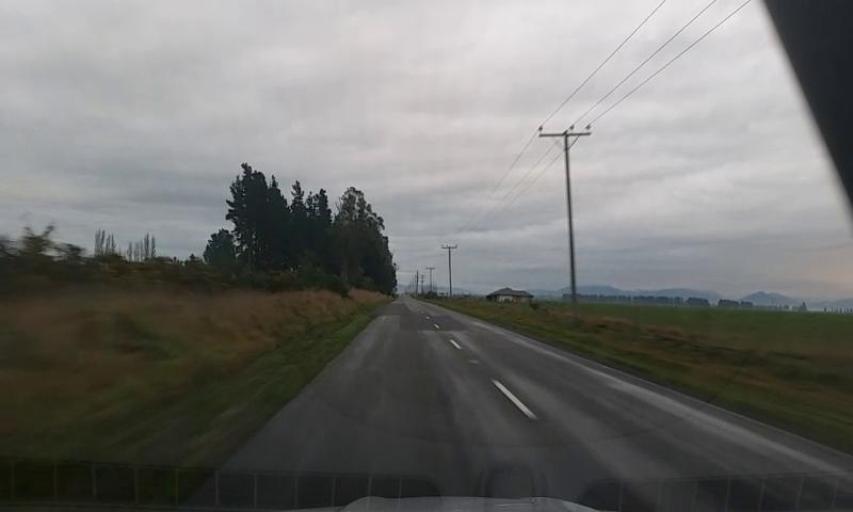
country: NZ
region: Canterbury
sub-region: Ashburton District
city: Ashburton
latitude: -43.7502
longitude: 171.8277
